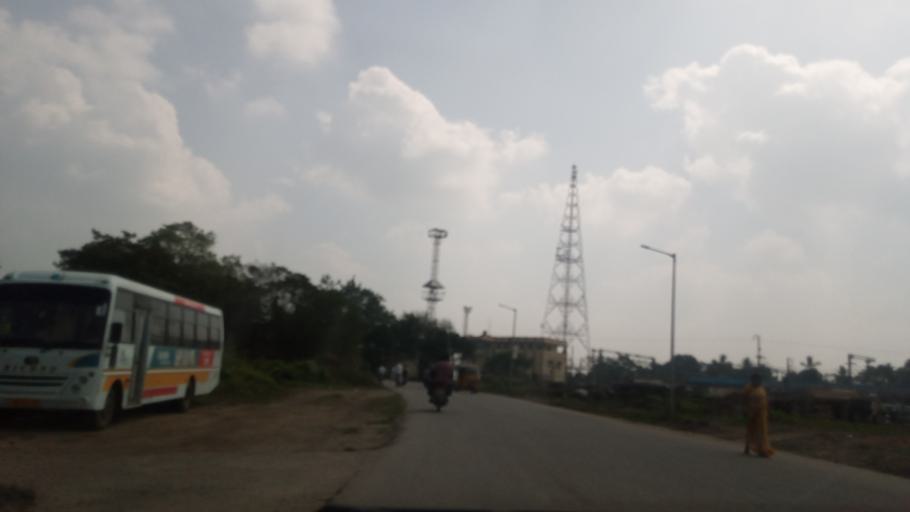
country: IN
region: Tamil Nadu
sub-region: Vellore
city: Arakkonam
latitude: 13.0826
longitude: 79.6653
